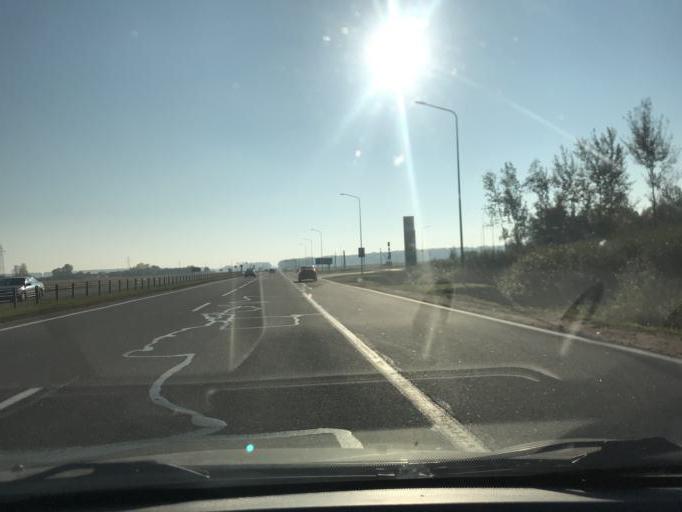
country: BY
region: Minsk
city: Dukora
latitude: 53.6349
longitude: 28.0117
